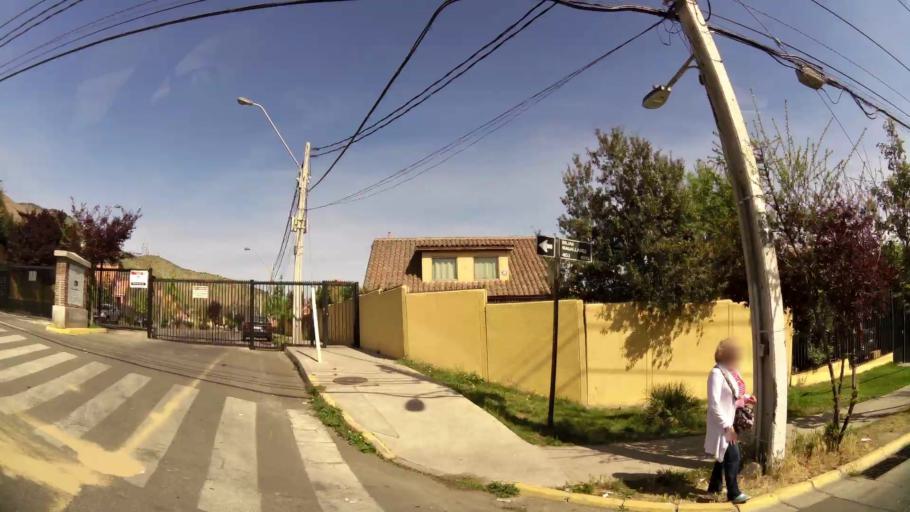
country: CL
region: Santiago Metropolitan
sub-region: Provincia de Cordillera
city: Puente Alto
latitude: -33.5357
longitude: -70.5479
